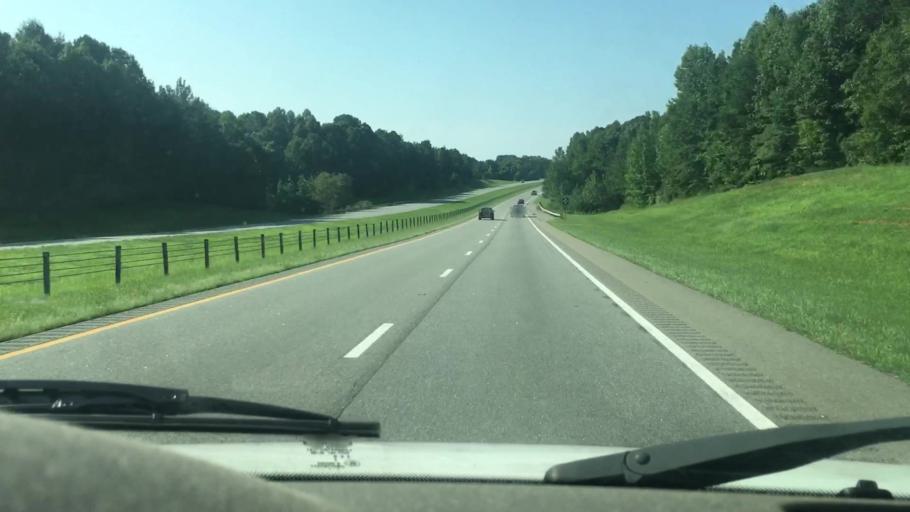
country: US
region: North Carolina
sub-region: Lincoln County
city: Lowesville
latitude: 35.3989
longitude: -80.9982
